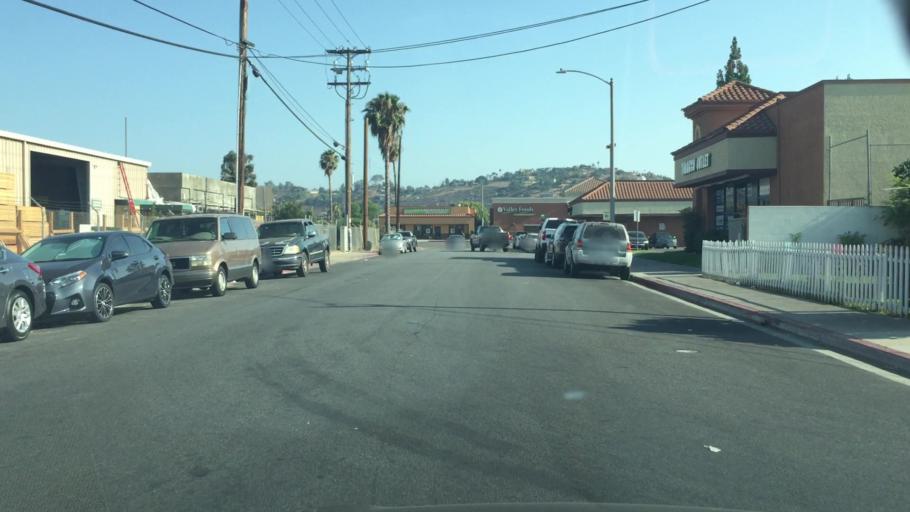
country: US
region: California
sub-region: San Diego County
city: Bostonia
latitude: 32.7961
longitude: -116.9380
